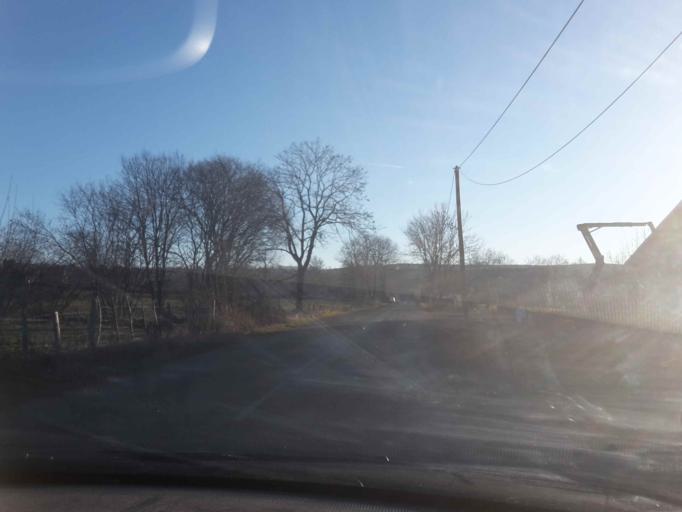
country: FR
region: Auvergne
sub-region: Departement du Cantal
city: Ydes
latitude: 45.2458
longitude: 2.5412
